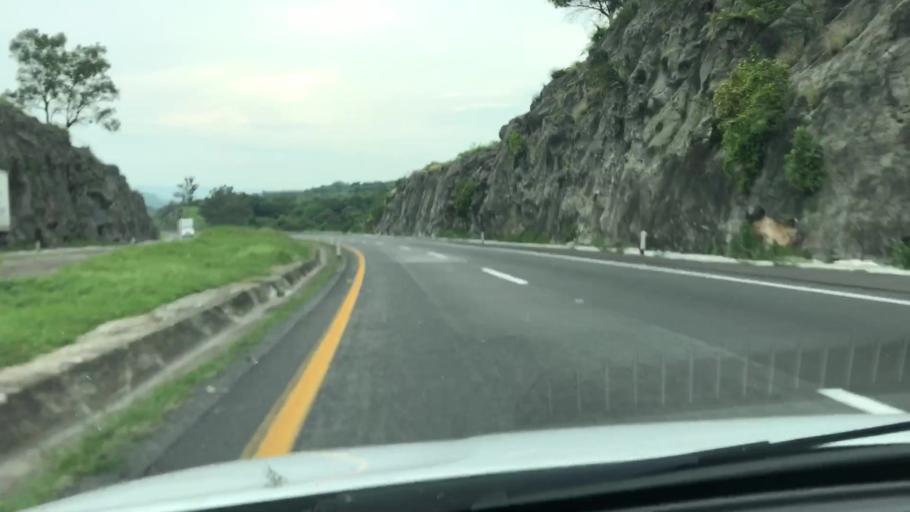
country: MX
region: Jalisco
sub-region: Zapotlan del Rey
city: Zapotlan del Rey
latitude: 20.5129
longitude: -102.9719
